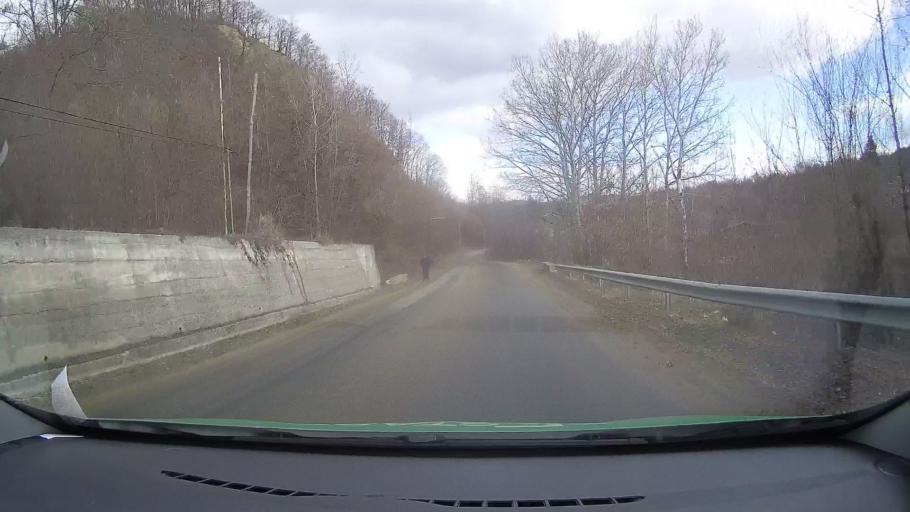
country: RO
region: Dambovita
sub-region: Comuna Buciumeni
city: Buciumeni
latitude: 45.1260
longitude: 25.4664
